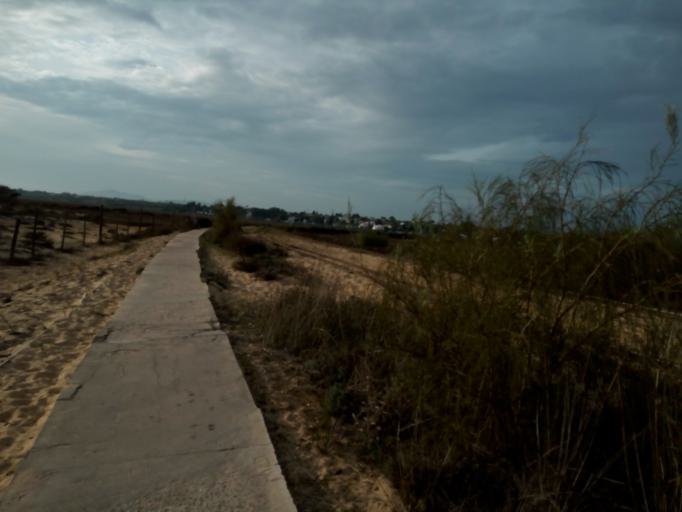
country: PT
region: Faro
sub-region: Tavira
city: Luz
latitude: 37.0890
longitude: -7.6691
